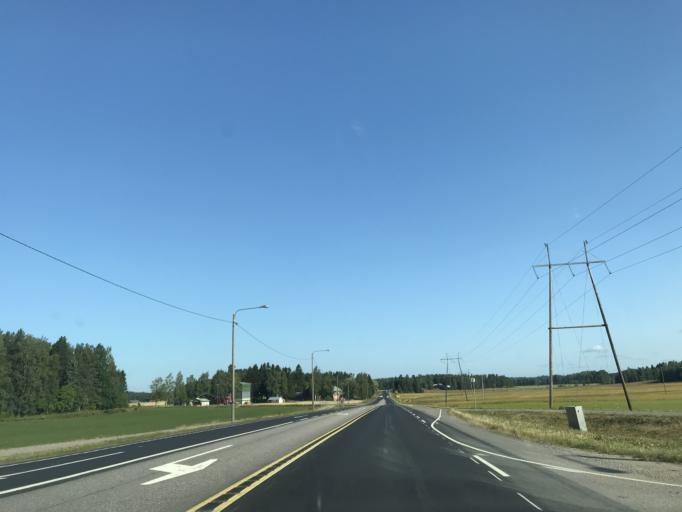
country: FI
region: Paijanne Tavastia
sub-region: Lahti
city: Lahti
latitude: 61.0912
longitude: 25.6493
